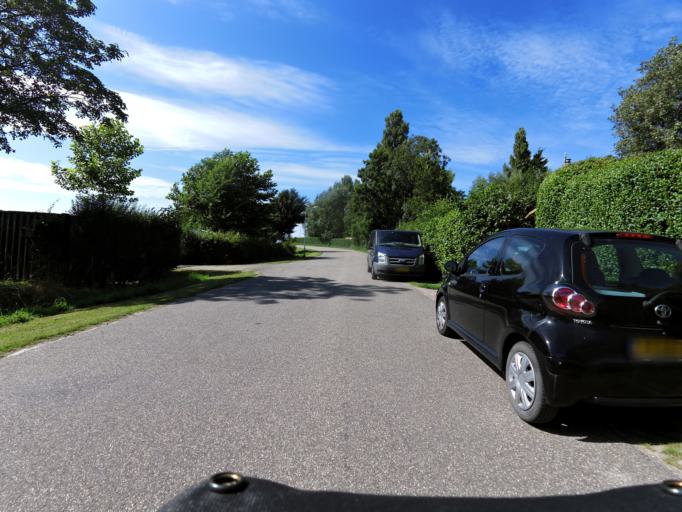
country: NL
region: Zeeland
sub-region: Gemeente Noord-Beveland
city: Kamperland
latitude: 51.5793
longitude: 3.6977
